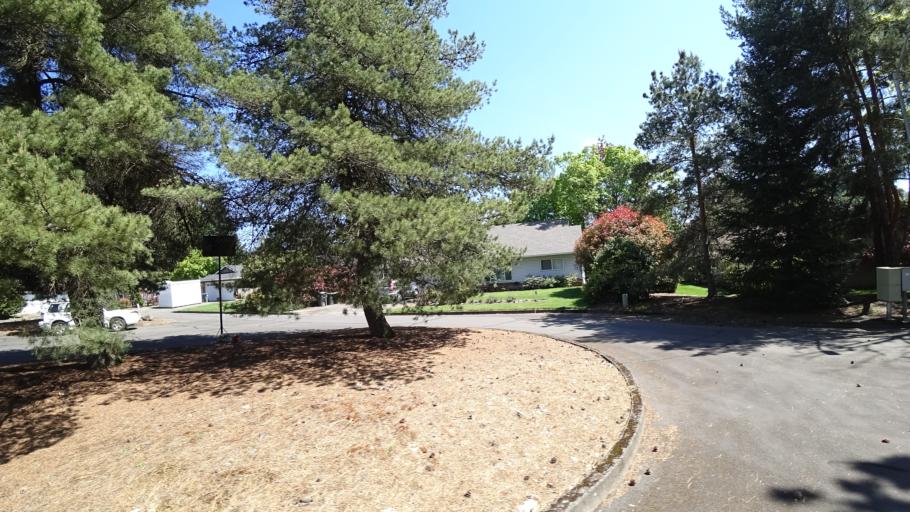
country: US
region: Oregon
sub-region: Washington County
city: Hillsboro
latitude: 45.5007
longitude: -122.9570
